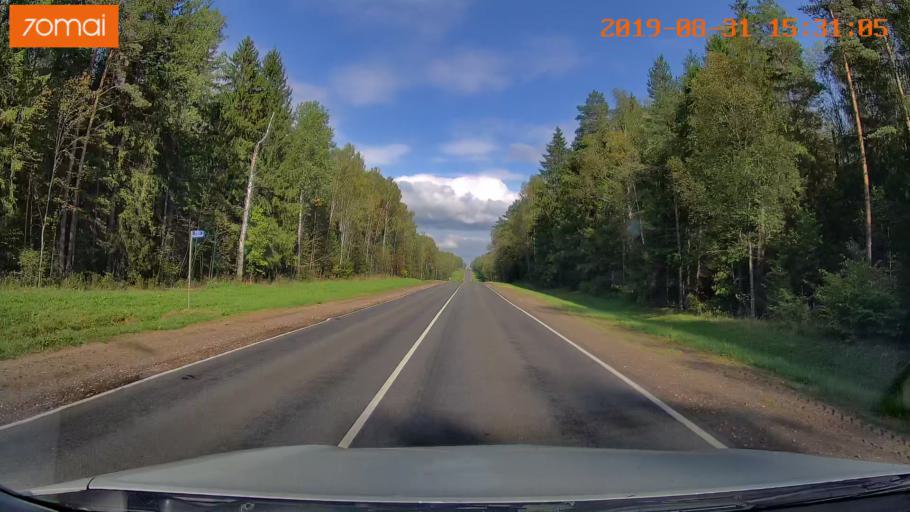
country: RU
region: Kaluga
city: Baryatino
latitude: 54.5800
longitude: 34.6459
